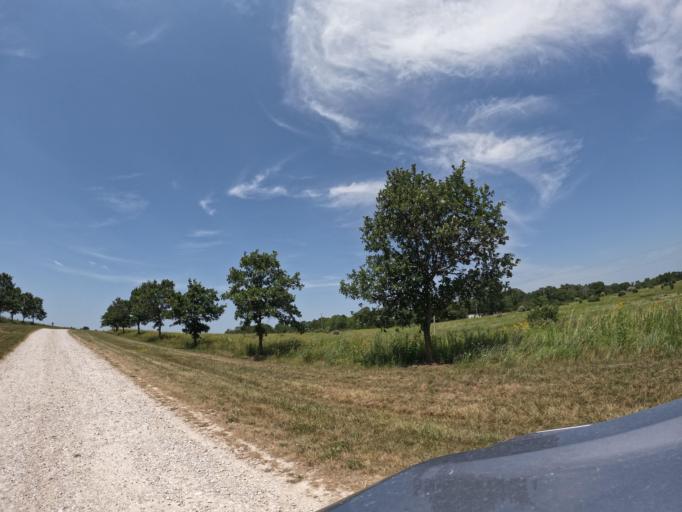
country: US
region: Iowa
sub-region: Henry County
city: Mount Pleasant
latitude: 40.9394
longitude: -91.5824
